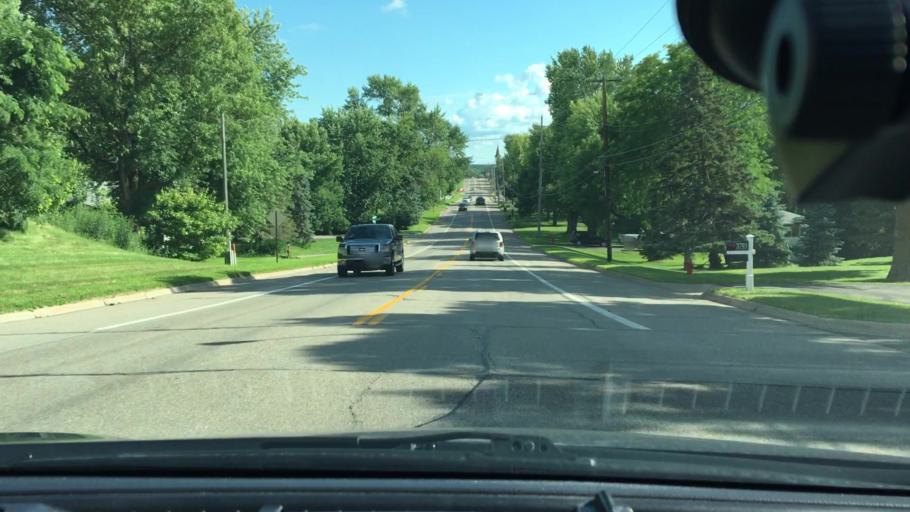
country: US
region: Minnesota
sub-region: Hennepin County
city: Saint Bonifacius
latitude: 44.9099
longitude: -93.7473
